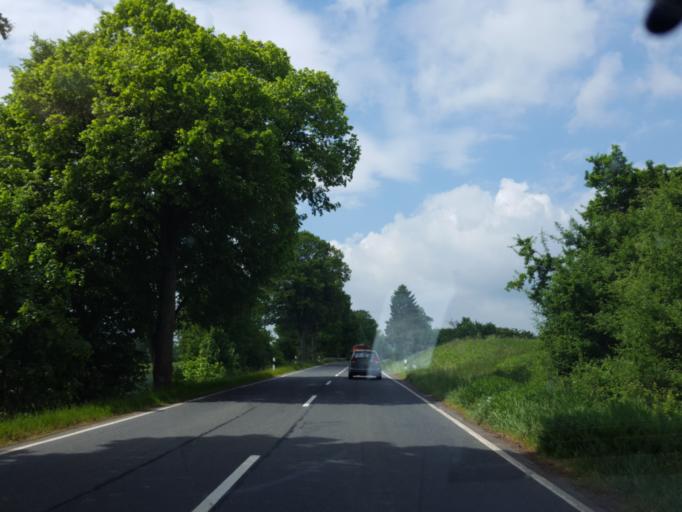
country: DE
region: Lower Saxony
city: Osterode am Harz
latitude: 51.7205
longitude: 10.2040
